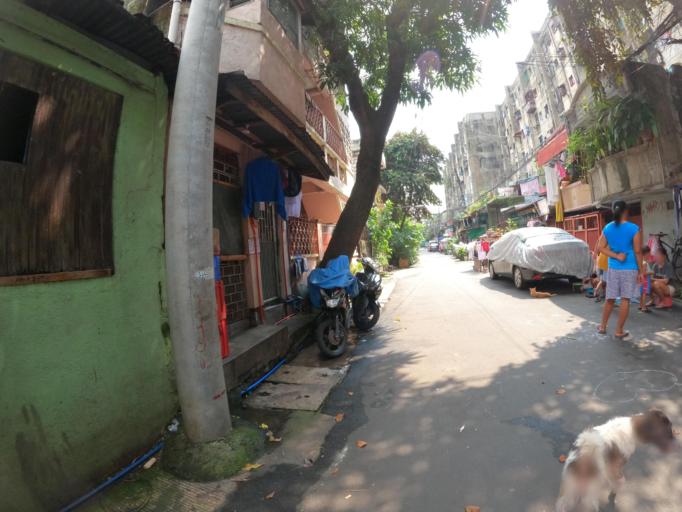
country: PH
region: Metro Manila
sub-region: San Juan
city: San Juan
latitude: 14.5870
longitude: 121.0109
